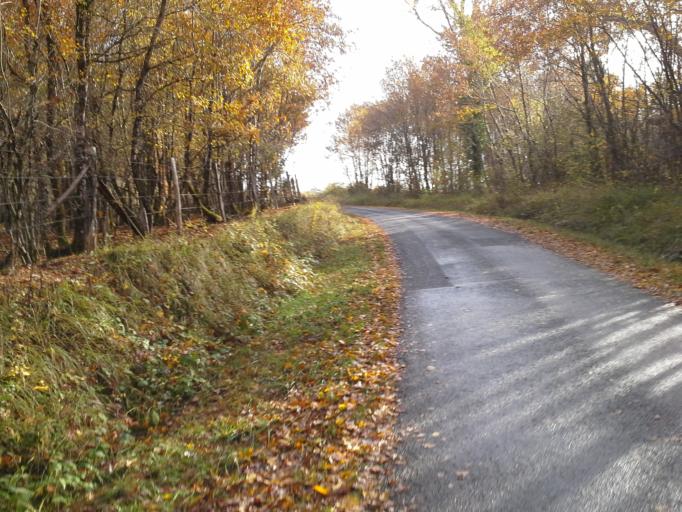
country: FR
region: Poitou-Charentes
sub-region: Departement de la Vienne
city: Pleumartin
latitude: 46.6400
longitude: 0.7628
